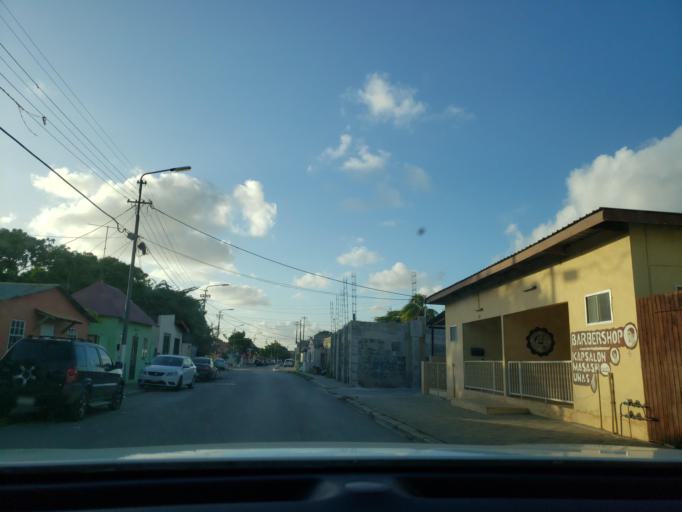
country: CW
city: Willemstad
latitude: 12.1007
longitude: -68.9194
